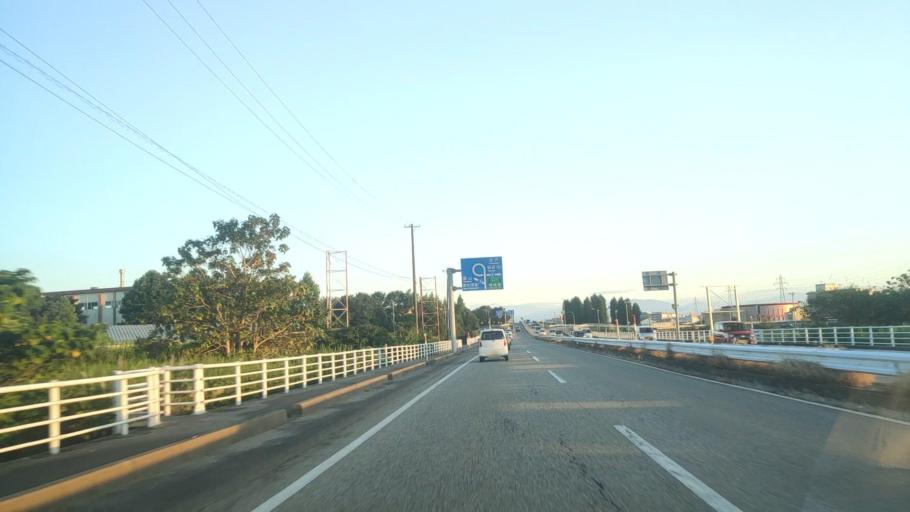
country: JP
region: Toyama
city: Takaoka
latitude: 36.7651
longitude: 137.0060
